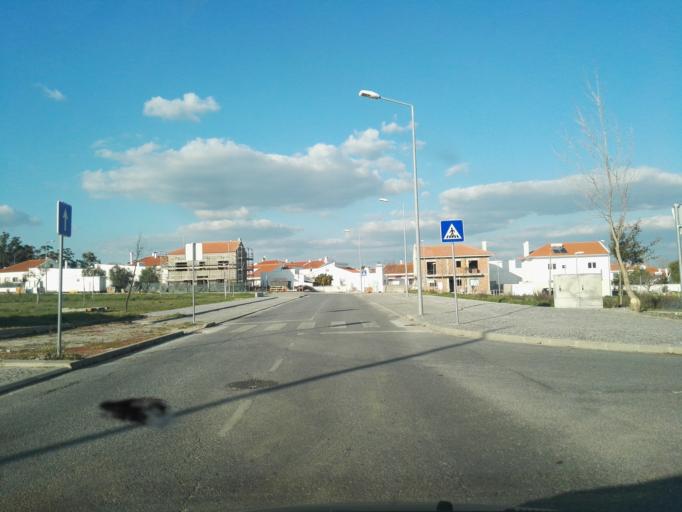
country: PT
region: Evora
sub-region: Evora
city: Evora
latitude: 38.5544
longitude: -7.9257
